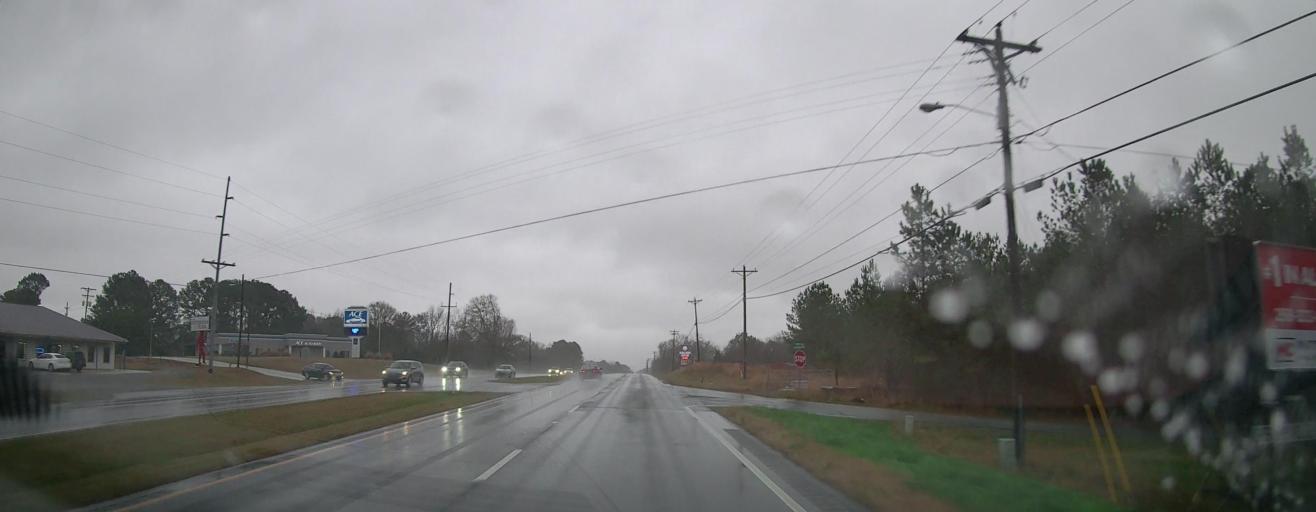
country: US
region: Alabama
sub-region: Morgan County
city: Hartselle
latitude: 34.4686
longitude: -86.9555
